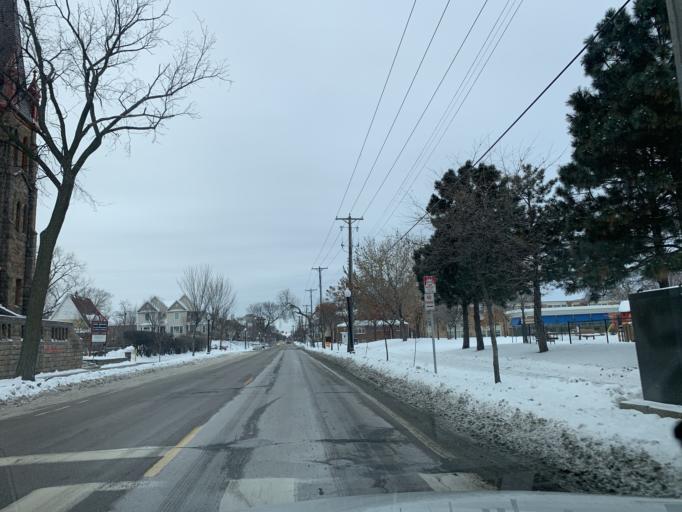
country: US
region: Minnesota
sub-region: Hennepin County
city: Minneapolis
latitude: 44.9592
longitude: -93.2486
